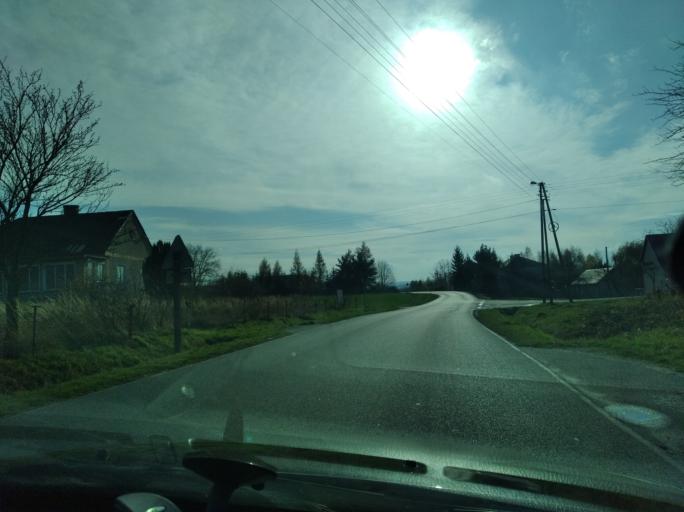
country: PL
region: Subcarpathian Voivodeship
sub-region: Powiat ropczycko-sedziszowski
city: Iwierzyce
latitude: 50.0749
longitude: 21.7523
